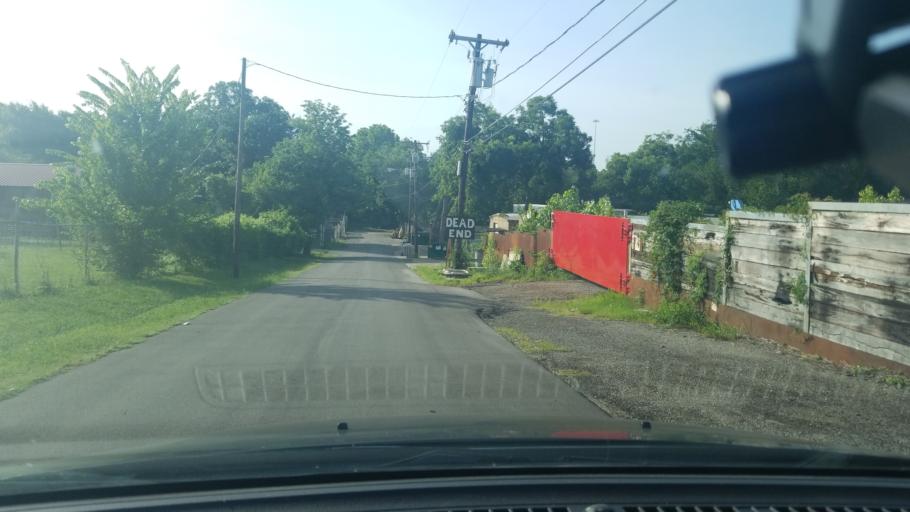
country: US
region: Texas
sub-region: Dallas County
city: Highland Park
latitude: 32.7978
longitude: -96.7153
